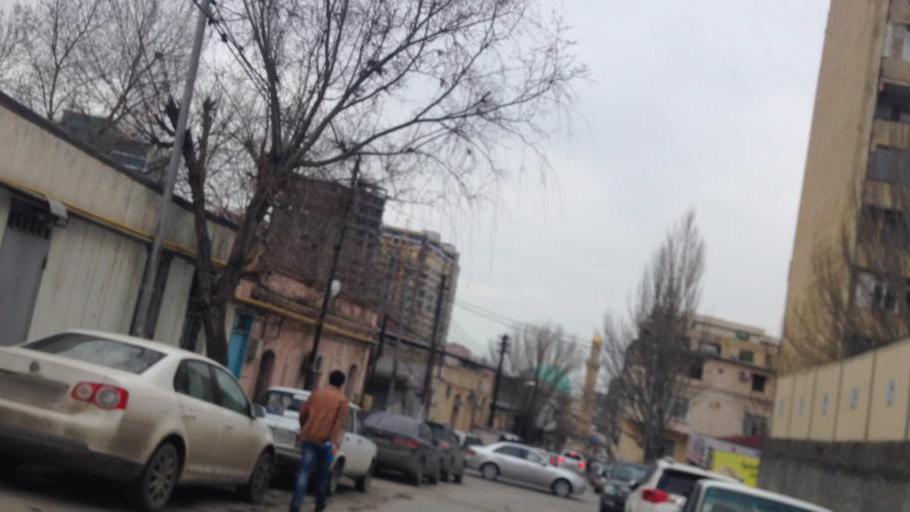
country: AZ
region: Baki
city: Badamdar
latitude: 40.3811
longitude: 49.8285
